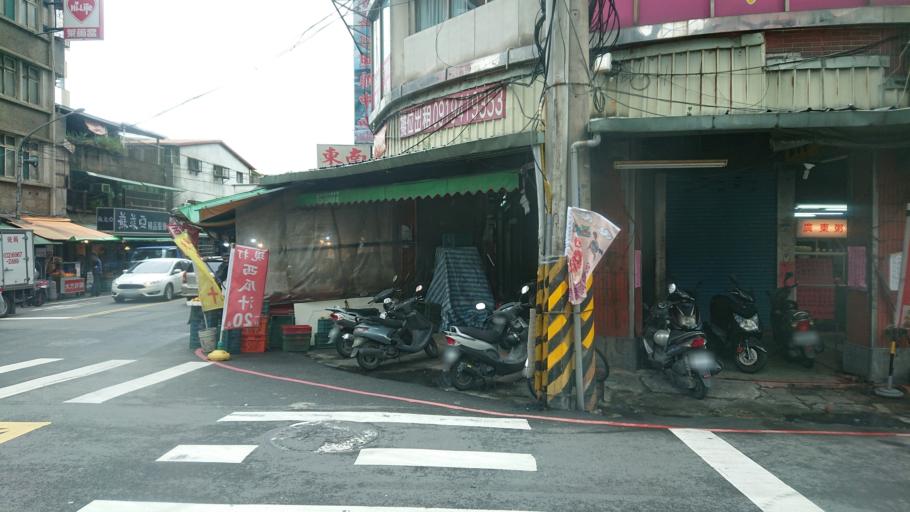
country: TW
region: Taipei
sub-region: Taipei
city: Banqiao
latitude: 24.9750
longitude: 121.4424
